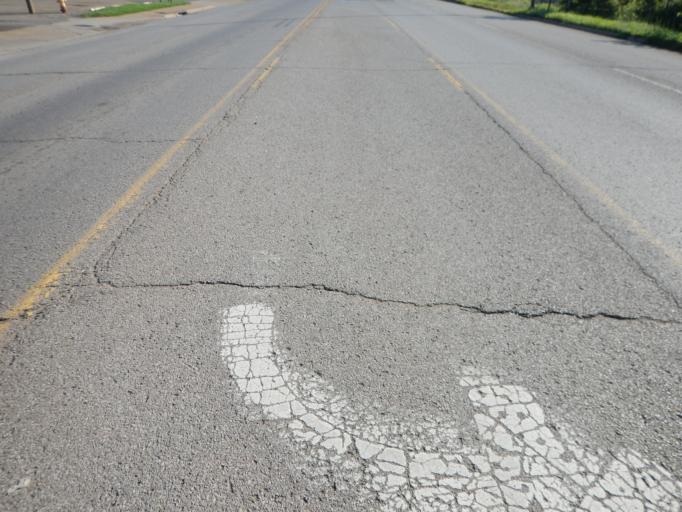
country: US
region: Ohio
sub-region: Muskingum County
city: South Zanesville
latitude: 39.9109
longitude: -82.0161
